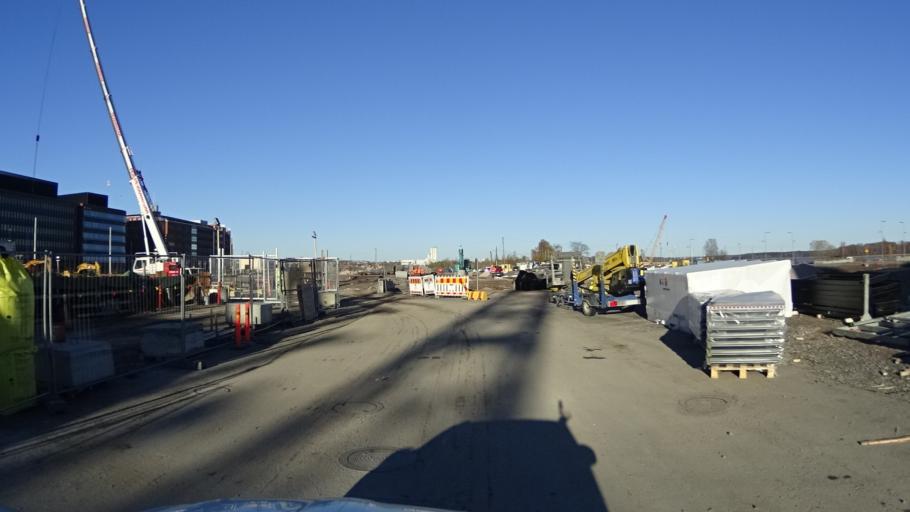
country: FI
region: Uusimaa
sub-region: Helsinki
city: Helsinki
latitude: 60.1885
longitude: 24.9798
